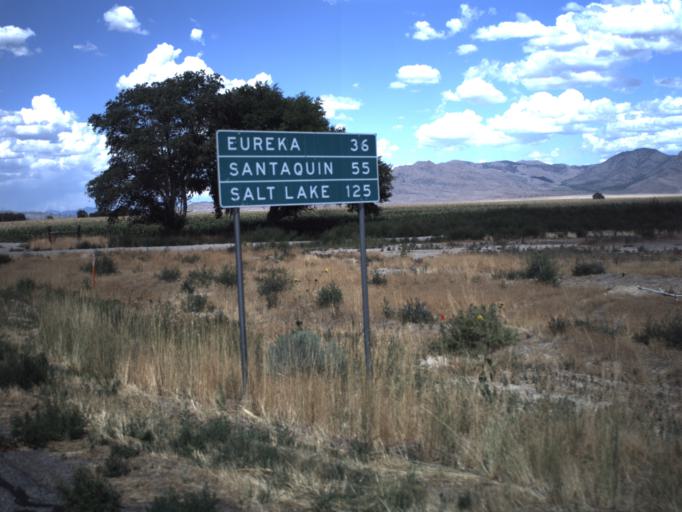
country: US
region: Utah
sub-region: Millard County
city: Delta
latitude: 39.5256
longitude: -112.3720
